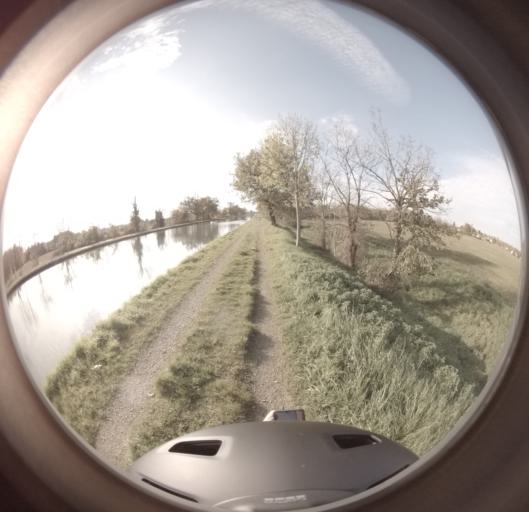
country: FR
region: Midi-Pyrenees
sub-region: Departement du Tarn-et-Garonne
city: Montbeton
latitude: 43.9839
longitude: 1.2718
